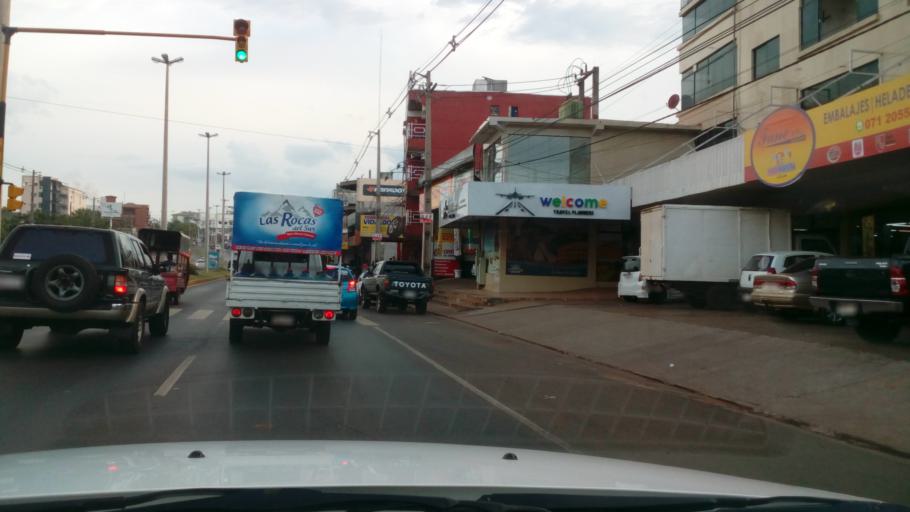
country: PY
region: Itapua
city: Encarnacion
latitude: -27.3459
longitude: -55.8581
